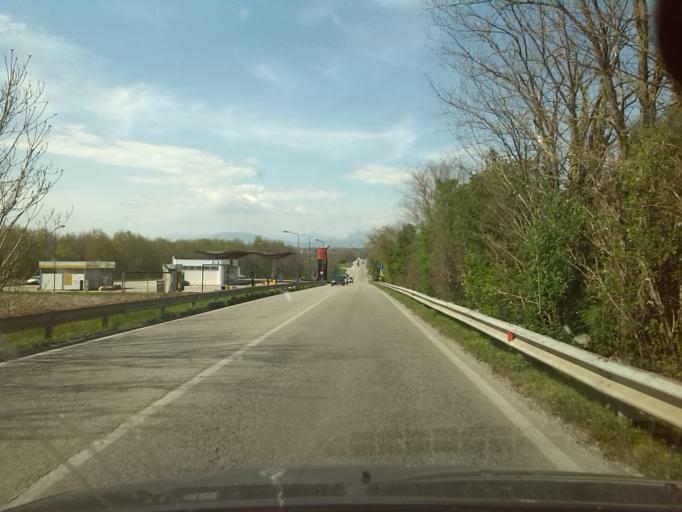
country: IT
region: Friuli Venezia Giulia
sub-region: Provincia di Udine
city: Colugna
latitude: 46.0995
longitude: 13.2076
